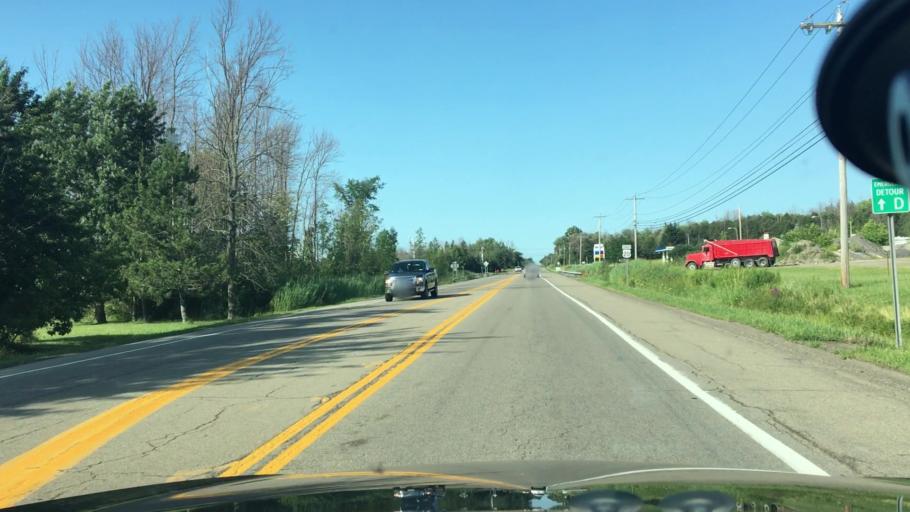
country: US
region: New York
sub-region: Erie County
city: Angola
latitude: 42.6529
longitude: -78.9808
